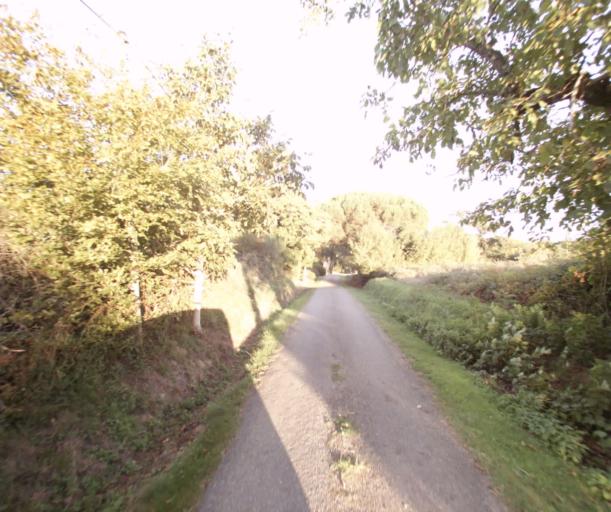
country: FR
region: Midi-Pyrenees
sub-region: Departement du Gers
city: Eauze
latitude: 43.8781
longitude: 0.0439
